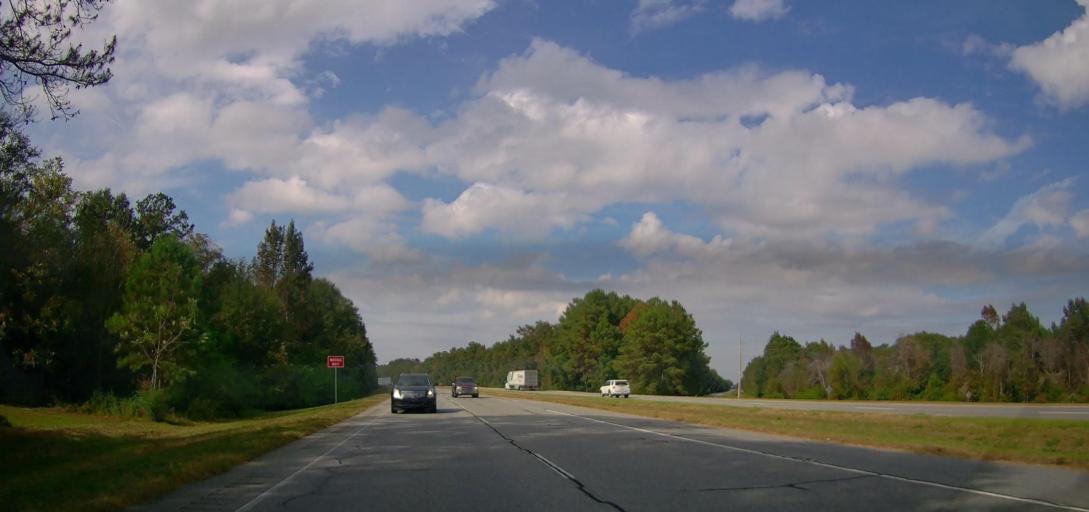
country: US
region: Georgia
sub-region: Mitchell County
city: Pelham
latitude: 31.1738
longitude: -84.1479
